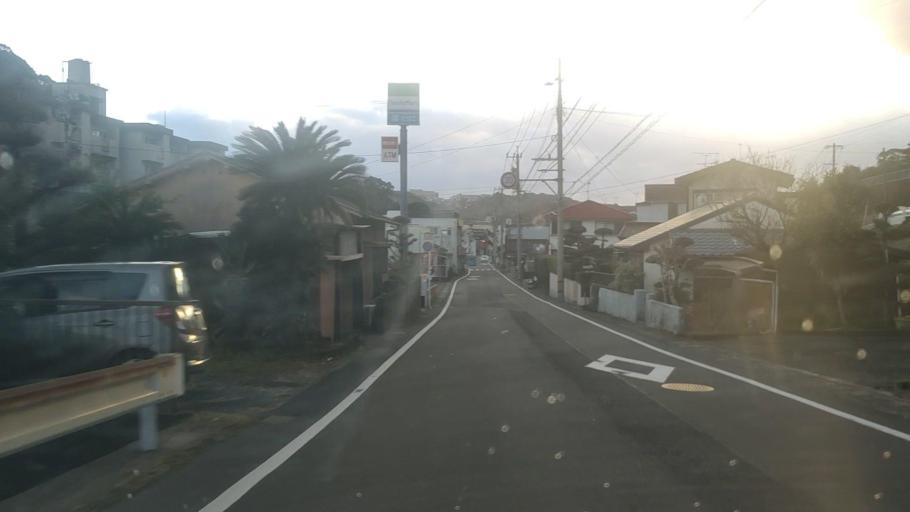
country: JP
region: Kagoshima
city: Kagoshima-shi
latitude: 31.6199
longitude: 130.5367
